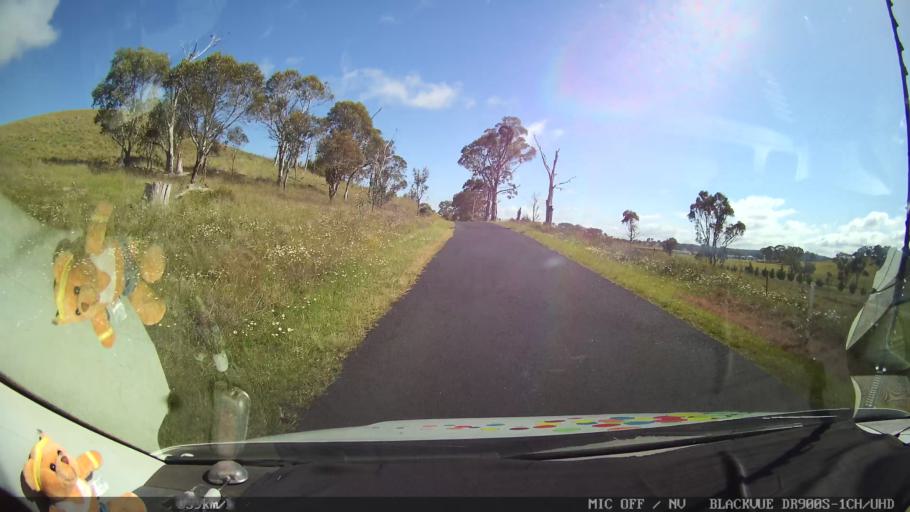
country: AU
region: New South Wales
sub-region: Guyra
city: Guyra
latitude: -30.1742
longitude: 151.6844
